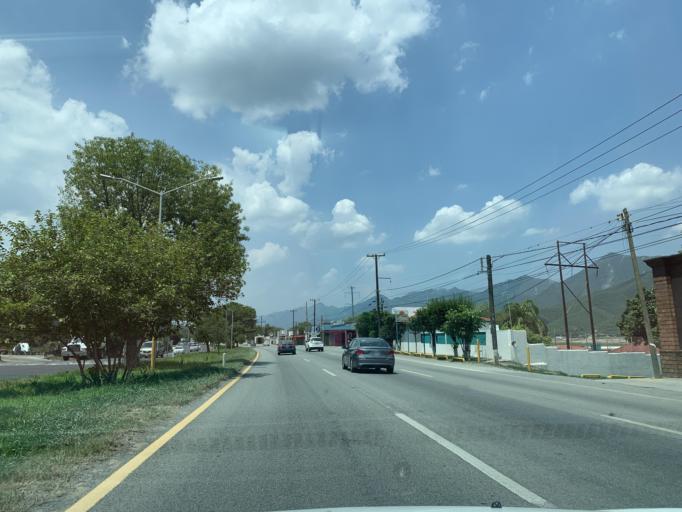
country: MX
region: Nuevo Leon
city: Santiago
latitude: 25.4162
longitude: -100.1419
